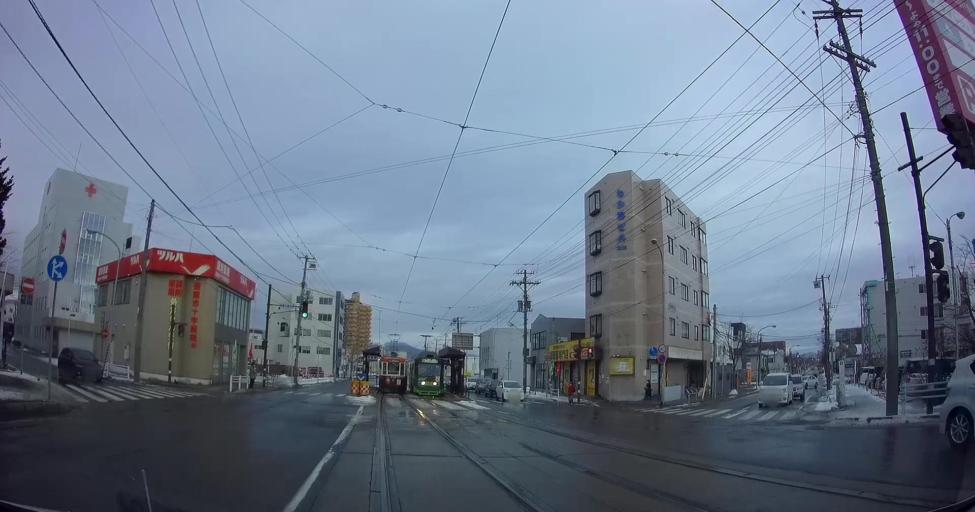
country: JP
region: Hokkaido
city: Hakodate
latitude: 41.7776
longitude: 140.7407
